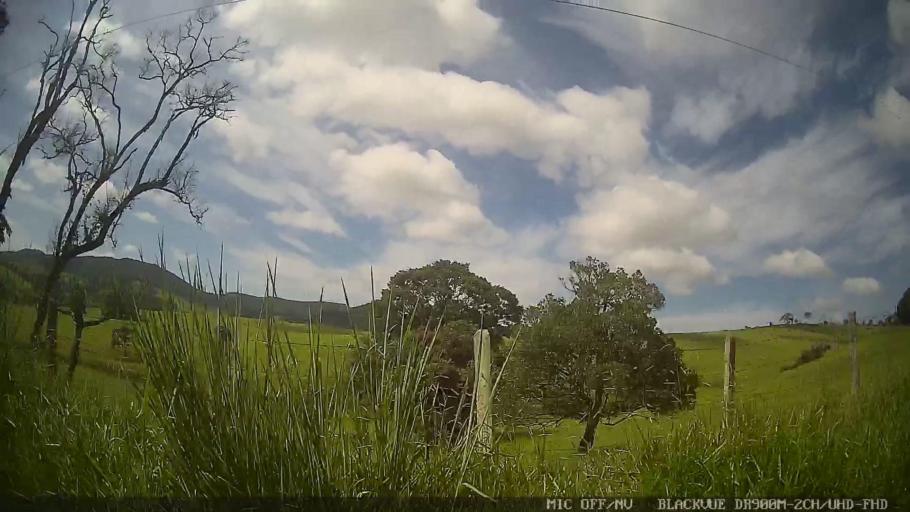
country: BR
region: Sao Paulo
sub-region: Braganca Paulista
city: Braganca Paulista
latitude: -22.9558
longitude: -46.6194
